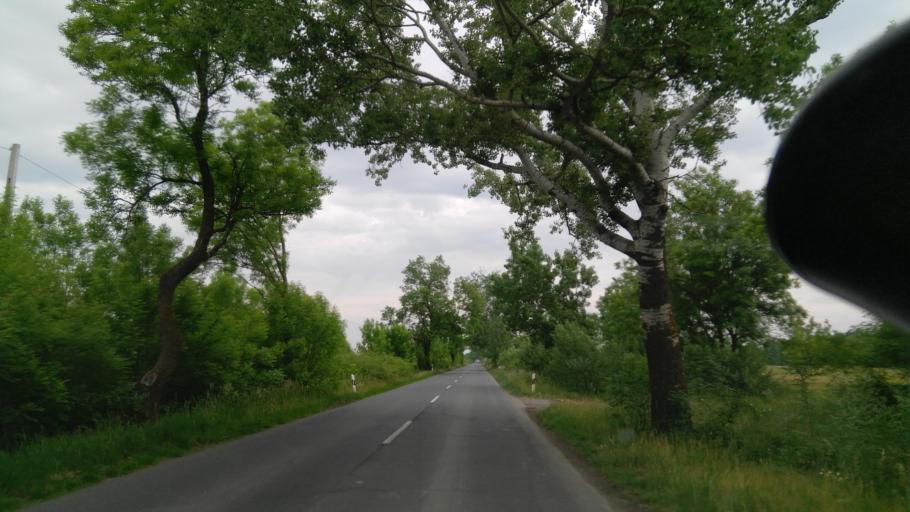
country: HU
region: Bekes
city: Veszto
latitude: 46.8951
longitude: 21.2477
